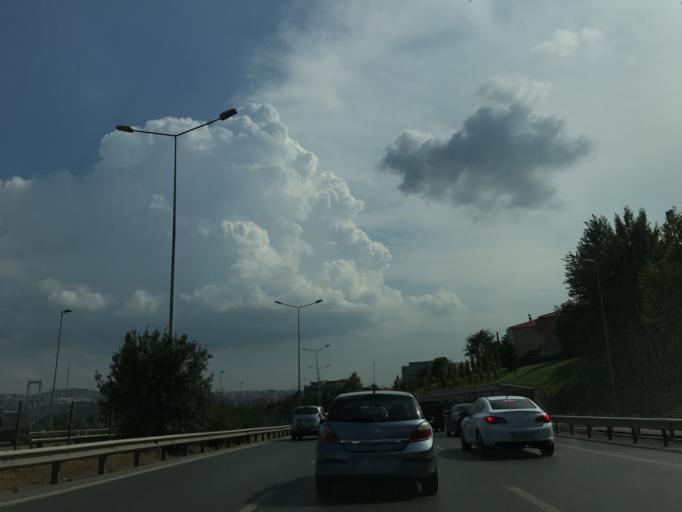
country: TR
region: Istanbul
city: Sisli
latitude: 41.0615
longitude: 29.0158
